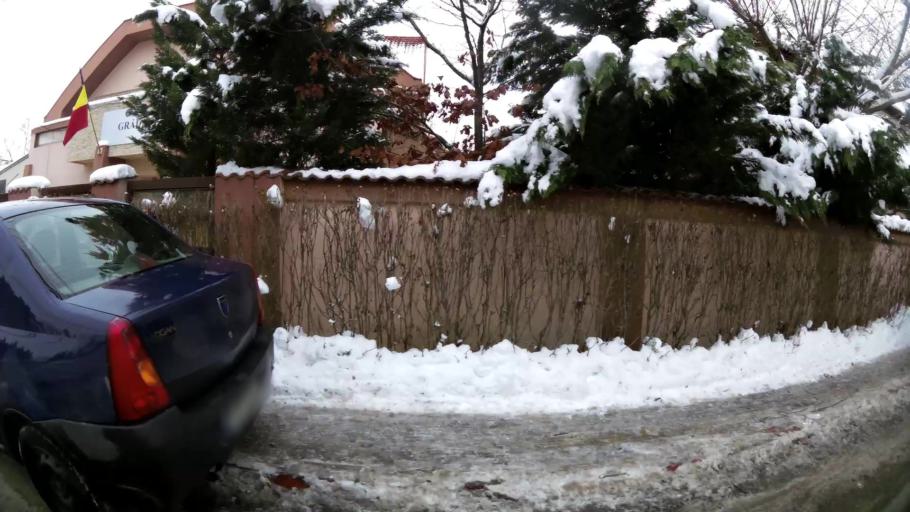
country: RO
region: Ilfov
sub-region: Comuna Otopeni
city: Otopeni
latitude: 44.5122
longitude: 26.1074
